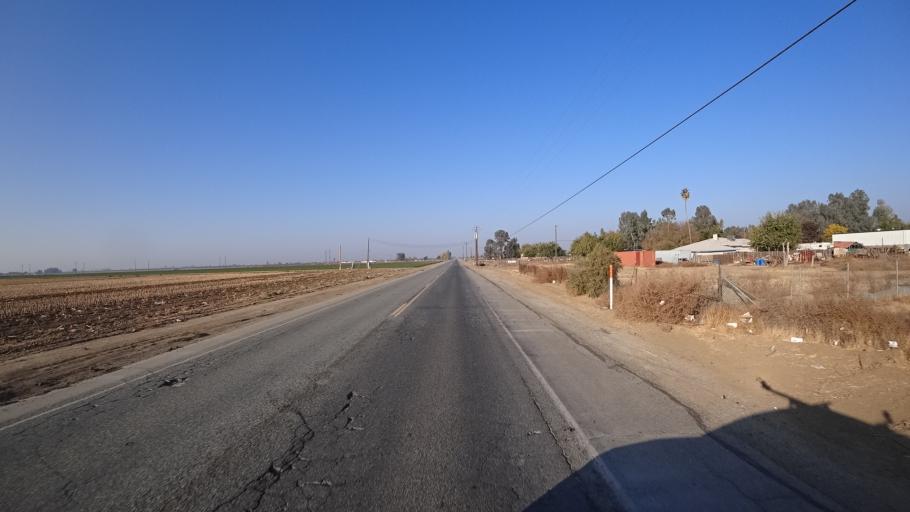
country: US
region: California
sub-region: Kern County
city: Greenfield
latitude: 35.2669
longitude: -118.9721
